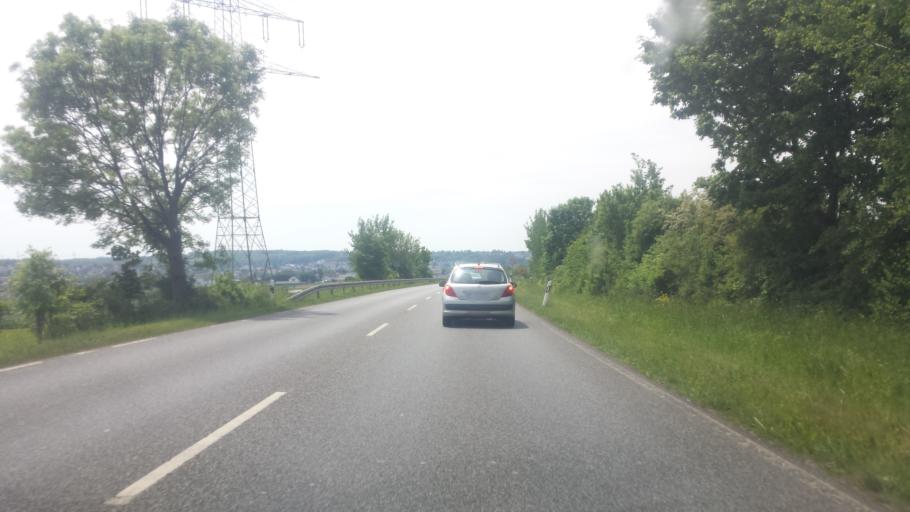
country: DE
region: Hesse
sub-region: Regierungsbezirk Darmstadt
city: Bad Vilbel
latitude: 50.2004
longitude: 8.7357
